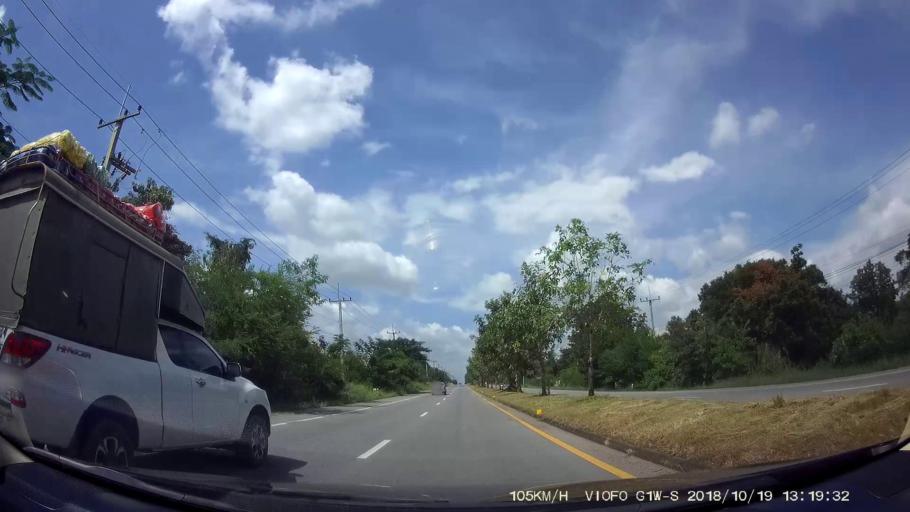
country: TH
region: Chaiyaphum
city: Chatturat
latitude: 15.4313
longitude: 101.8308
